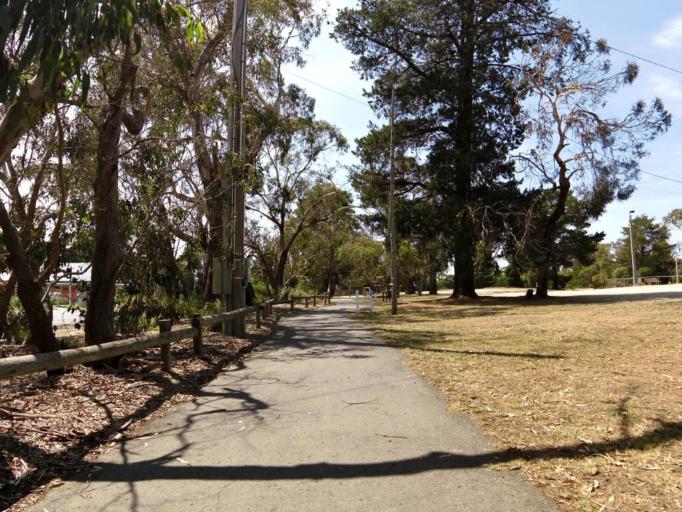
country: AU
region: Victoria
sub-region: Mornington Peninsula
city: Crib Point
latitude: -38.3372
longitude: 145.1775
